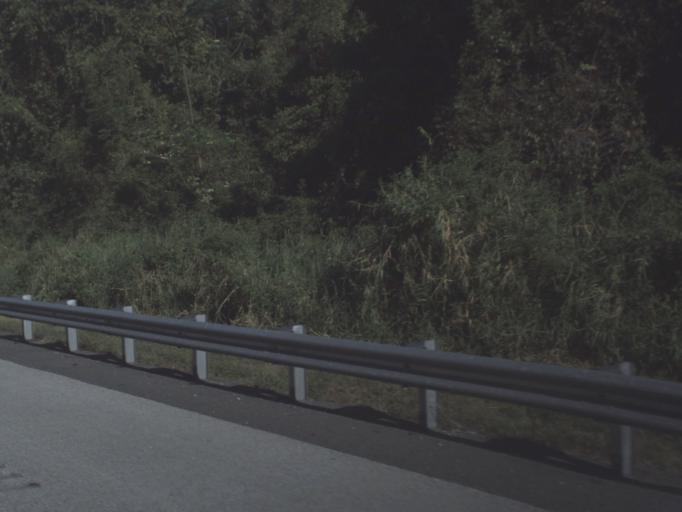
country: US
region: Florida
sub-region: Sumter County
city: Wildwood
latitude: 28.8477
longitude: -82.0784
